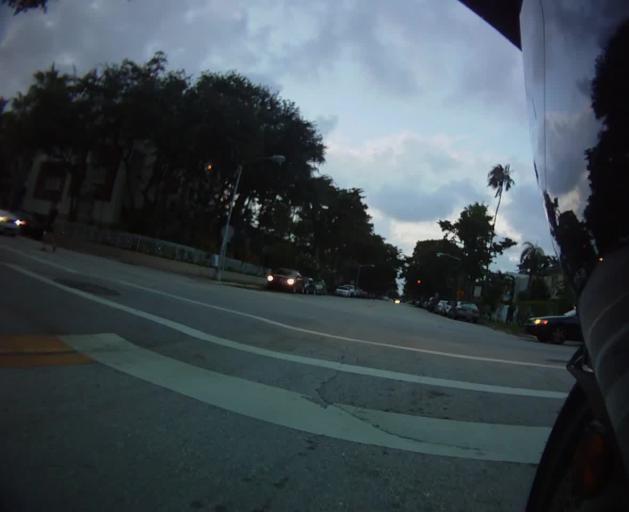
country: US
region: Florida
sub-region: Miami-Dade County
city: Miami Beach
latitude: 25.7782
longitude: -80.1384
